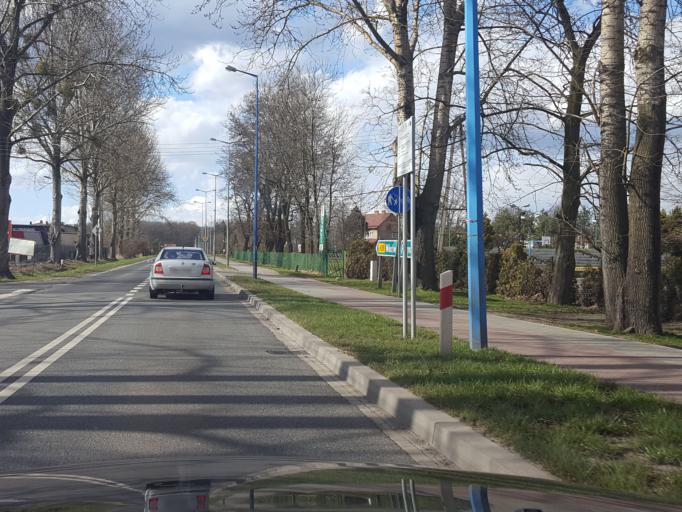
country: PL
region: Silesian Voivodeship
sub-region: Powiat pszczynski
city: Kobior
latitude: 50.0631
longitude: 18.9212
